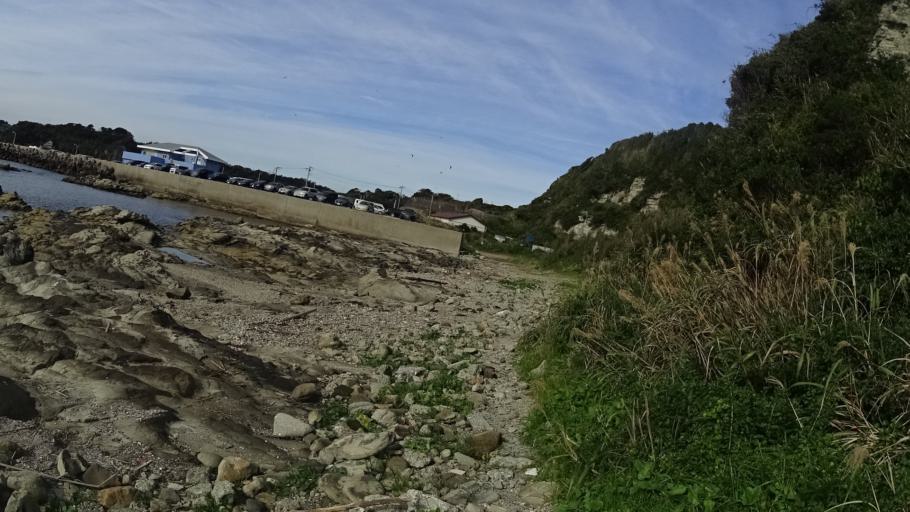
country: JP
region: Kanagawa
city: Miura
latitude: 35.1421
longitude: 139.6693
